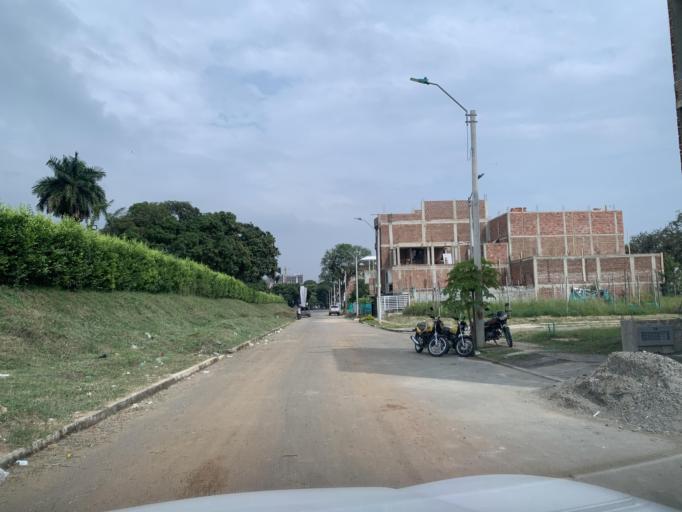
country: CO
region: Valle del Cauca
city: Cali
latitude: 3.3927
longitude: -76.5217
